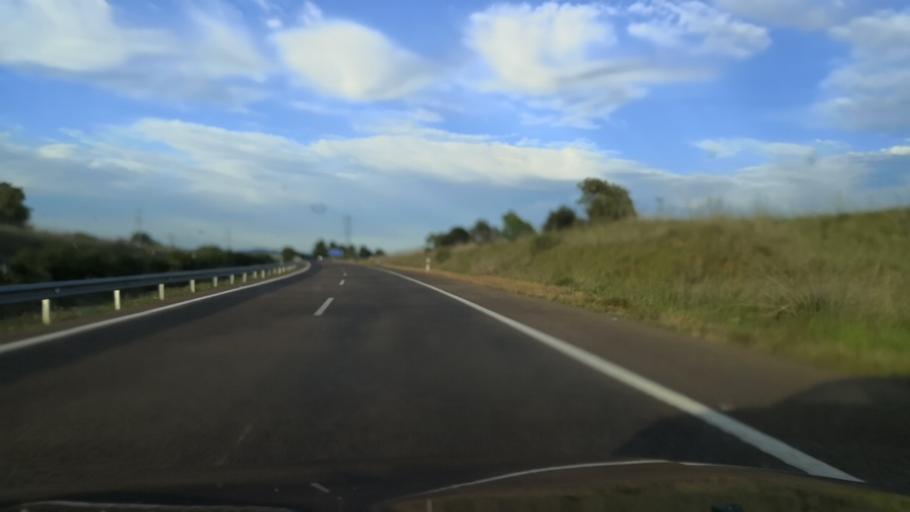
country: ES
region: Extremadura
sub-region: Provincia de Badajoz
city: Arroyo de San Servan
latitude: 38.8686
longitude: -6.4958
